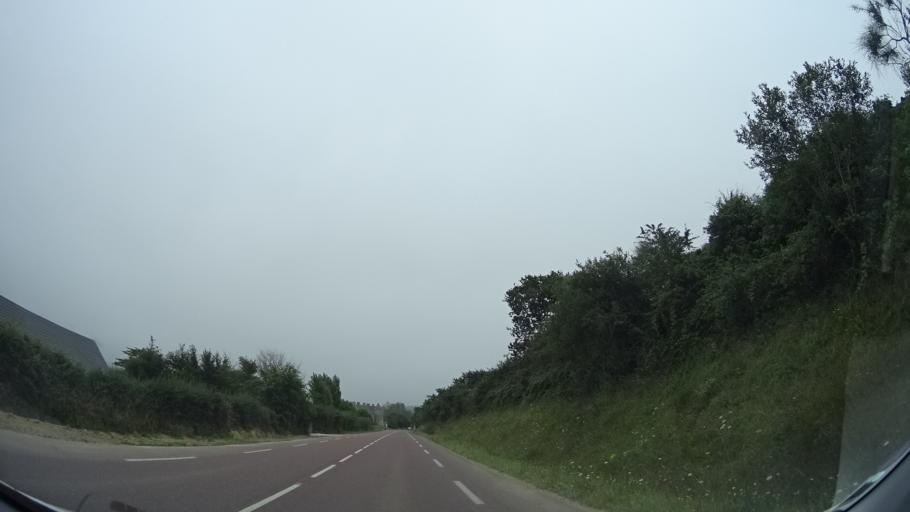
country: FR
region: Lower Normandy
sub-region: Departement de la Manche
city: Flamanville
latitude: 49.5417
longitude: -1.8395
